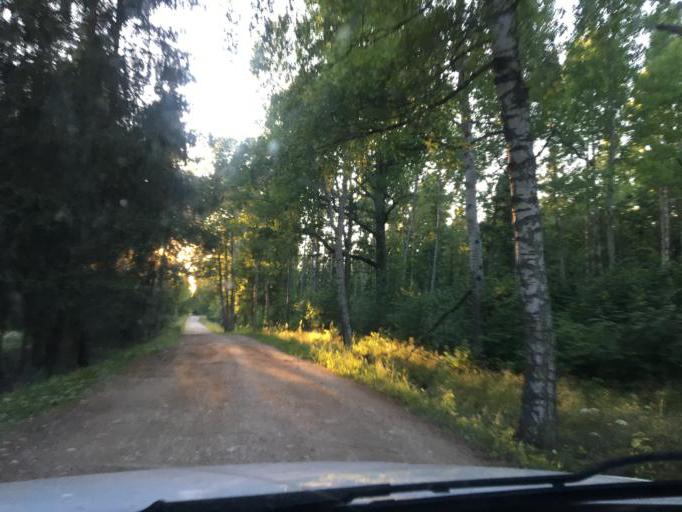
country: LV
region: Kuldigas Rajons
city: Kuldiga
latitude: 56.9799
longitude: 22.0287
